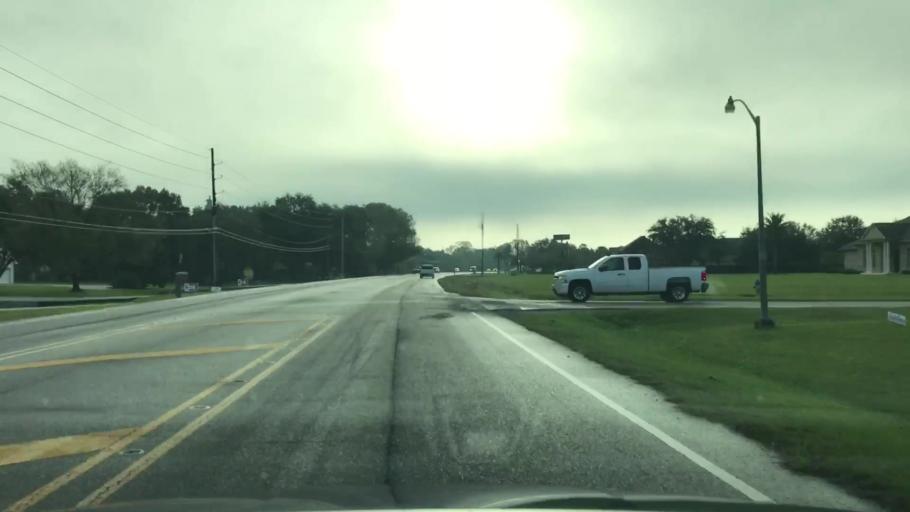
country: US
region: Louisiana
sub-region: Terrebonne Parish
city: Bayou Cane
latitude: 29.6141
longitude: -90.7849
